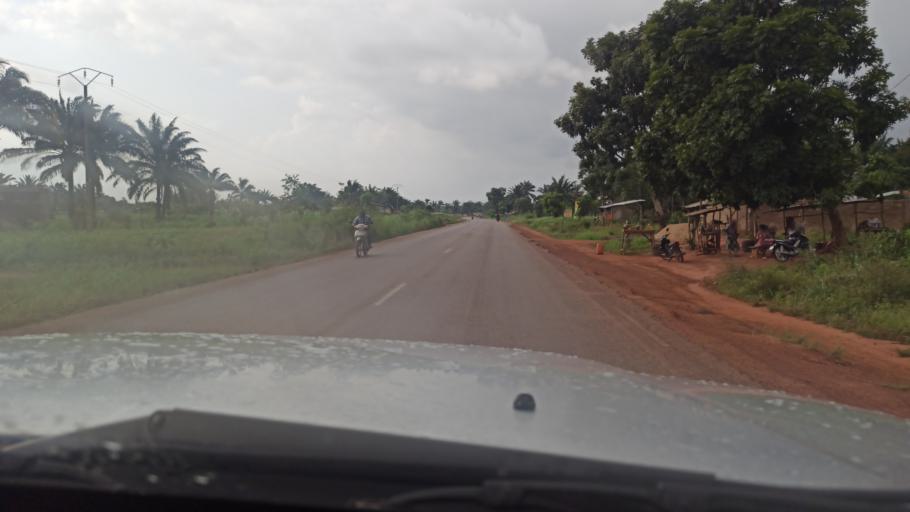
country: BJ
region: Queme
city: Porto-Novo
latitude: 6.5680
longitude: 2.5787
